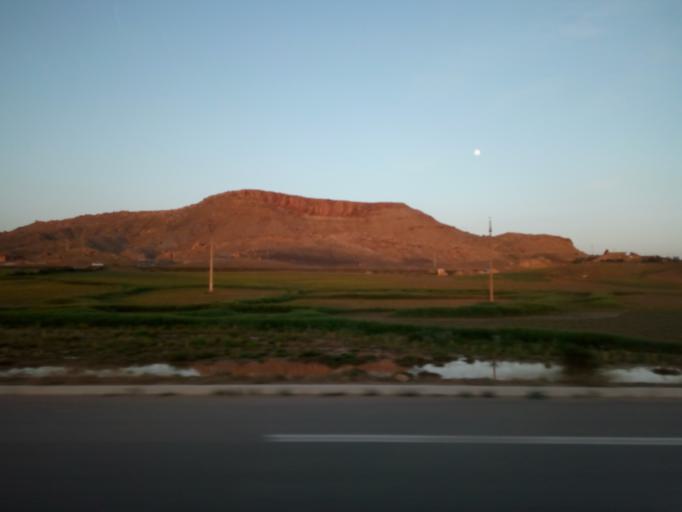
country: DZ
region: Medea
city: Ksar el Boukhari
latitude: 35.8146
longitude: 2.7664
